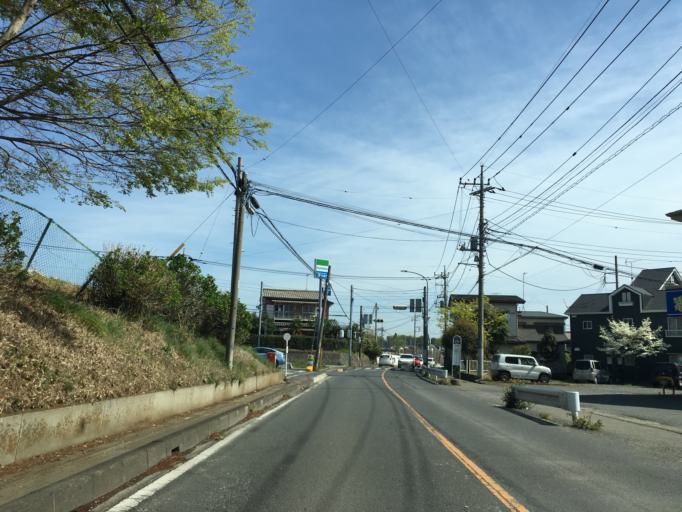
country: JP
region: Saitama
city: Hasuda
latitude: 35.9904
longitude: 139.6730
